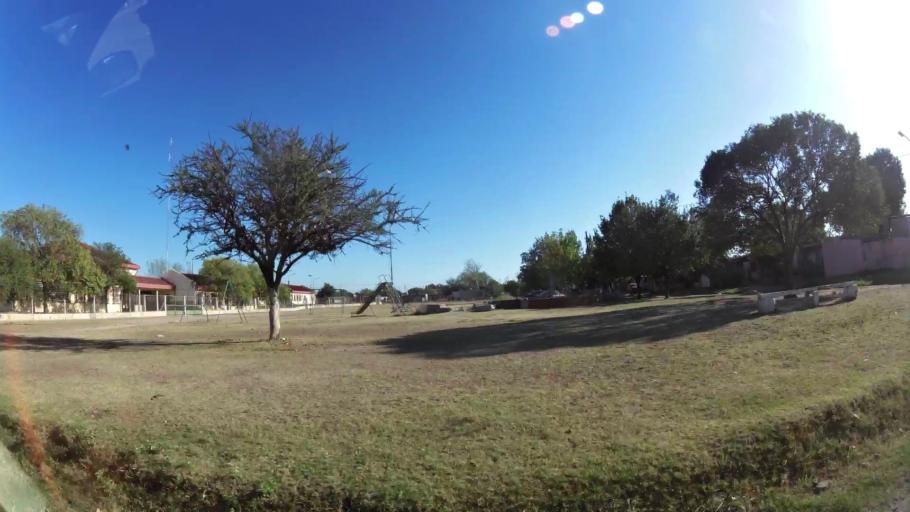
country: AR
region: Cordoba
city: Villa Allende
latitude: -31.3338
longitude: -64.2417
